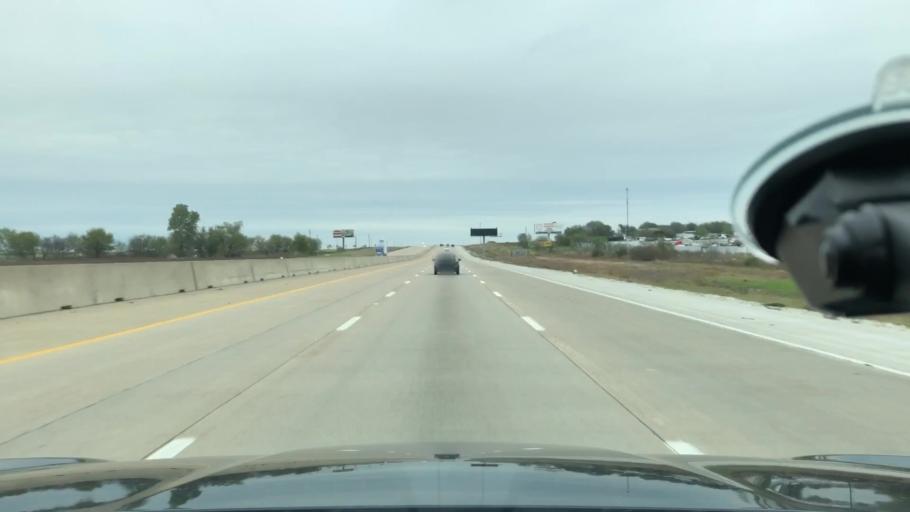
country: US
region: Texas
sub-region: Ellis County
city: Nash
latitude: 32.3106
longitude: -96.8625
